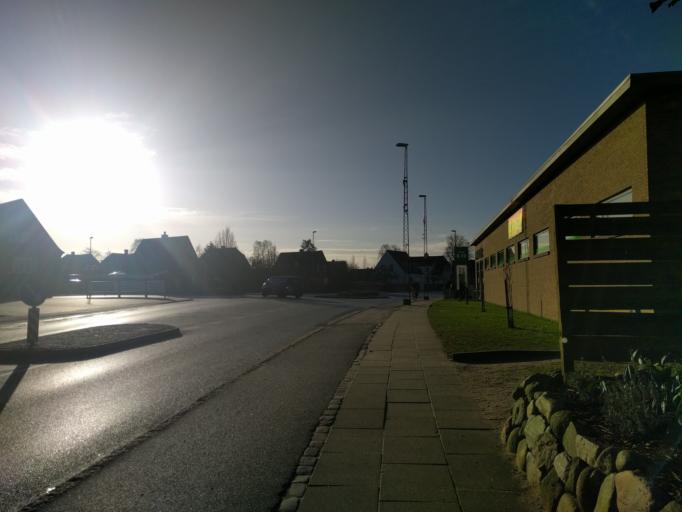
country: DK
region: Central Jutland
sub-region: Viborg Kommune
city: Viborg
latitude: 56.4606
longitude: 9.4167
